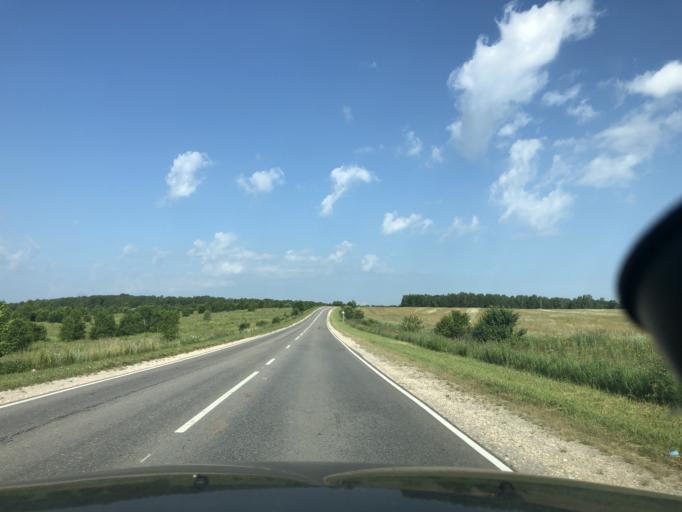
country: RU
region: Tula
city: Dubna
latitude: 54.1317
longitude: 37.0358
